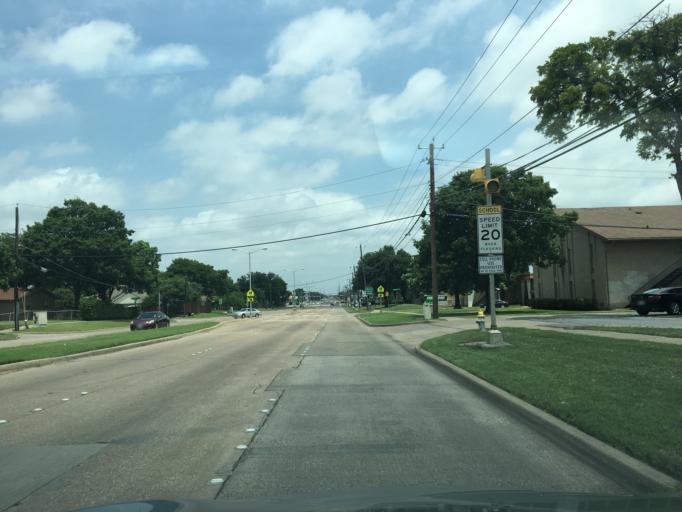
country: US
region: Texas
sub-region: Dallas County
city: Garland
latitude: 32.9132
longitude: -96.6828
